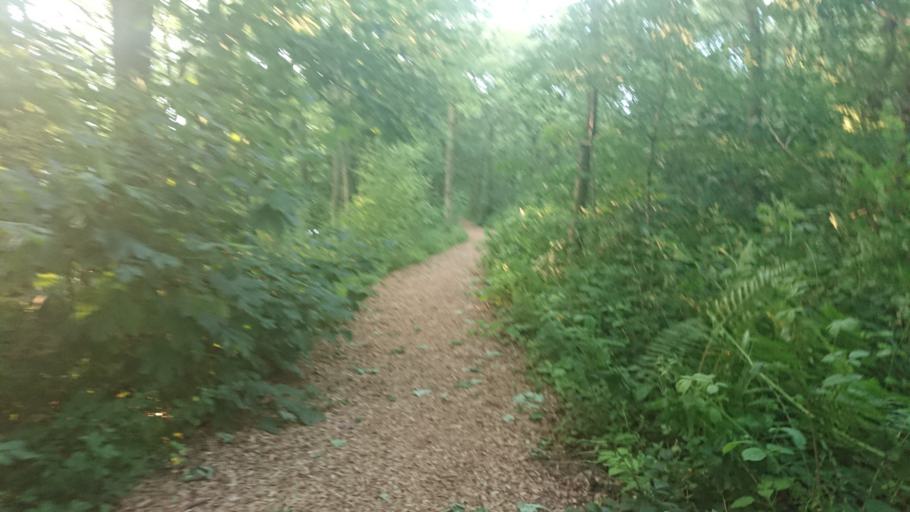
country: GB
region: England
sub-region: Lancashire
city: Galgate
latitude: 54.0058
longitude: -2.7825
